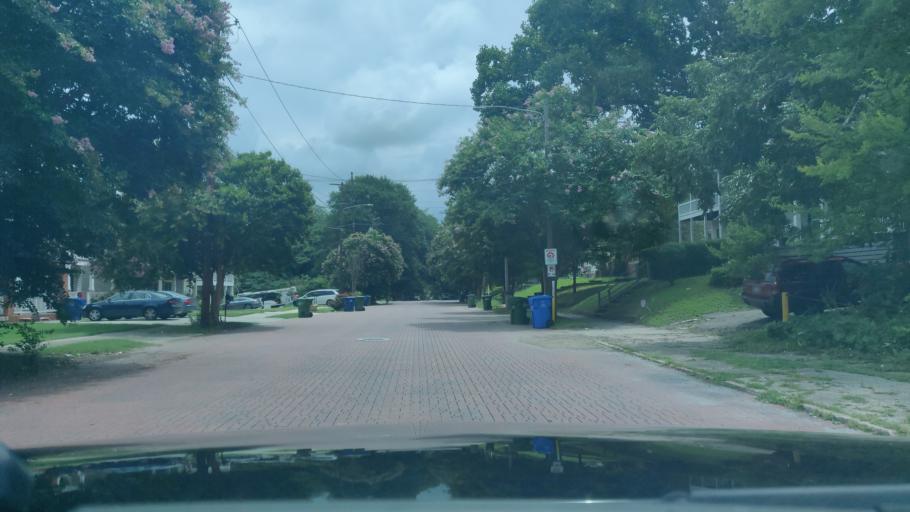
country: US
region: Georgia
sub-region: Fulton County
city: Atlanta
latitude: 33.7304
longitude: -84.3874
